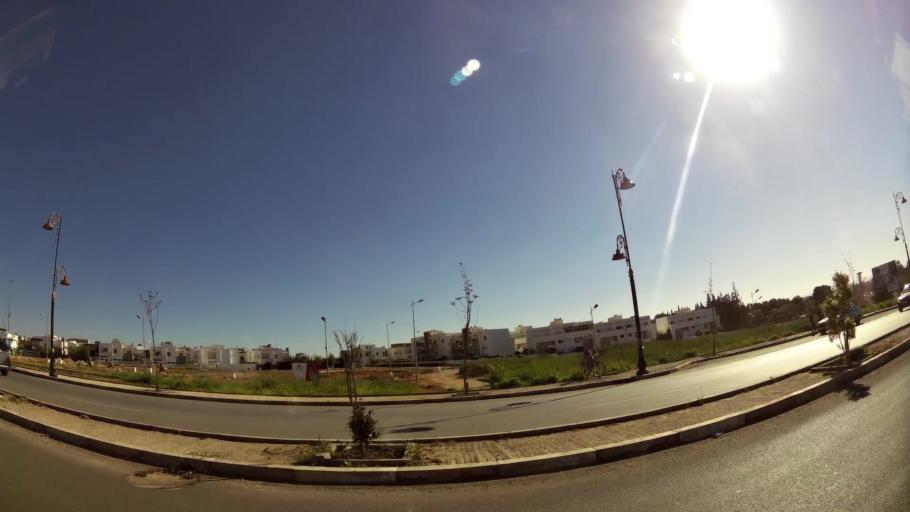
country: MA
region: Fes-Boulemane
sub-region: Fes
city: Oulad Tayeb
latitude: 33.9903
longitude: -5.0144
